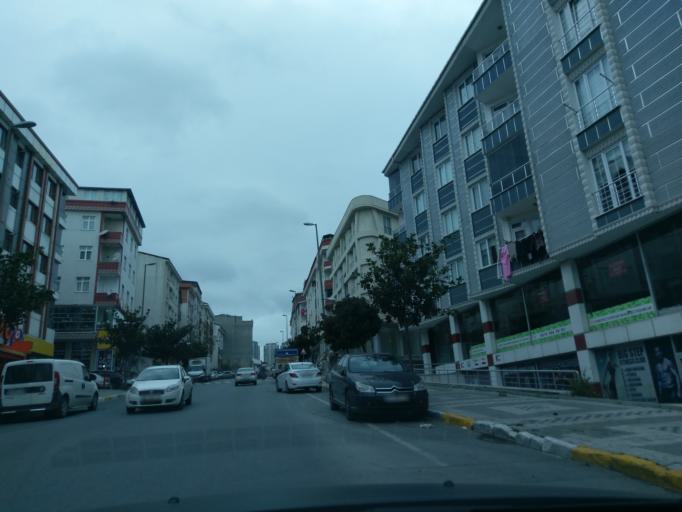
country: TR
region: Istanbul
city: Esenyurt
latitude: 41.0145
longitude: 28.6659
